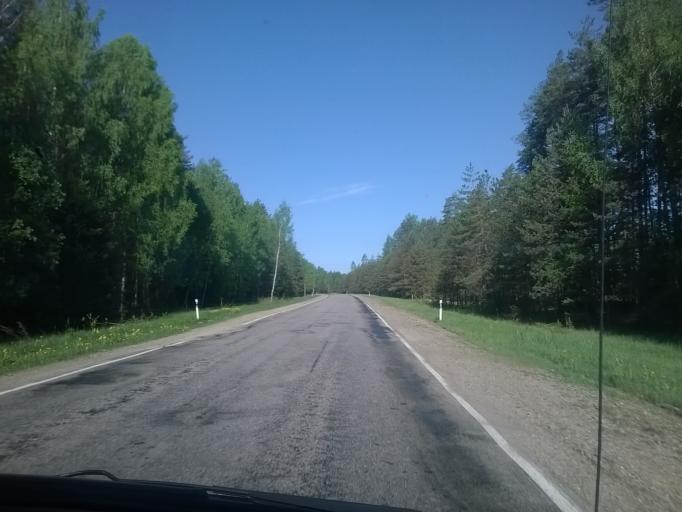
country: LV
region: Strenci
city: Seda
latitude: 57.6226
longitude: 25.7800
